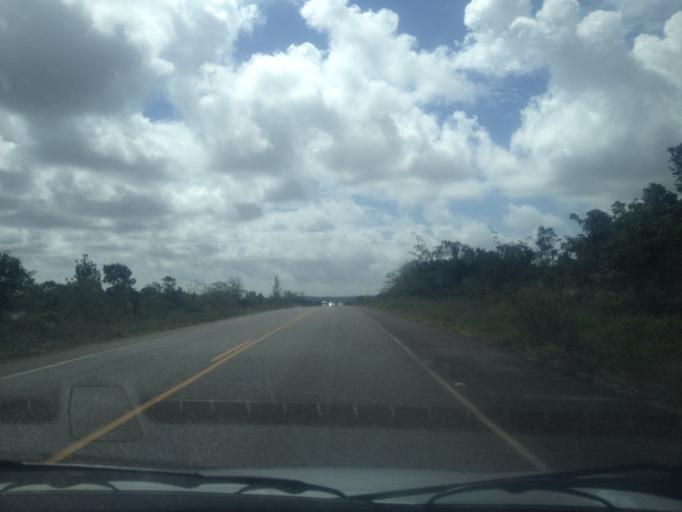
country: BR
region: Bahia
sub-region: Entre Rios
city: Entre Rios
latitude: -12.2634
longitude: -37.8713
